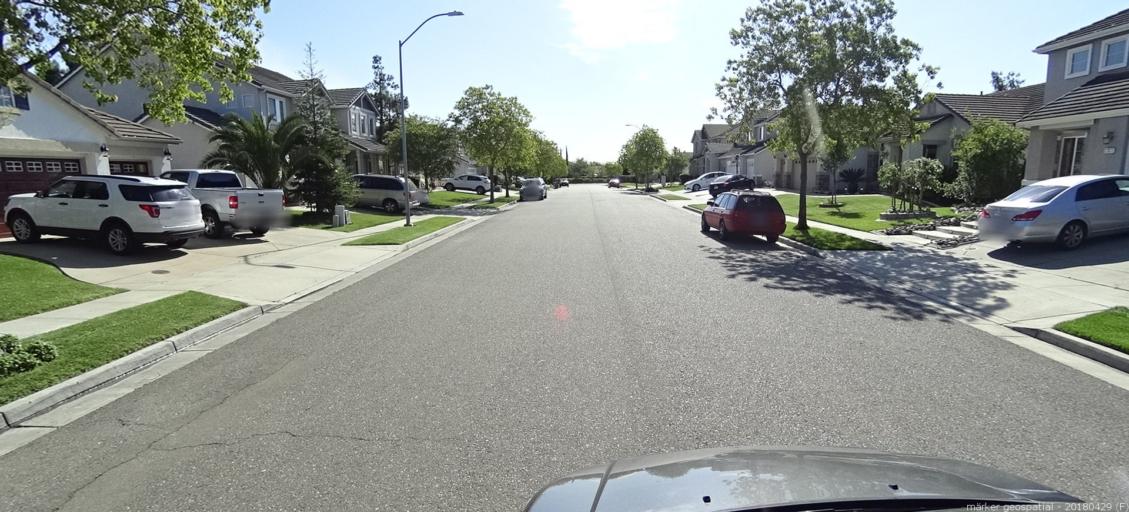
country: US
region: California
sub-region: Yolo County
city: West Sacramento
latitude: 38.5362
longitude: -121.5782
